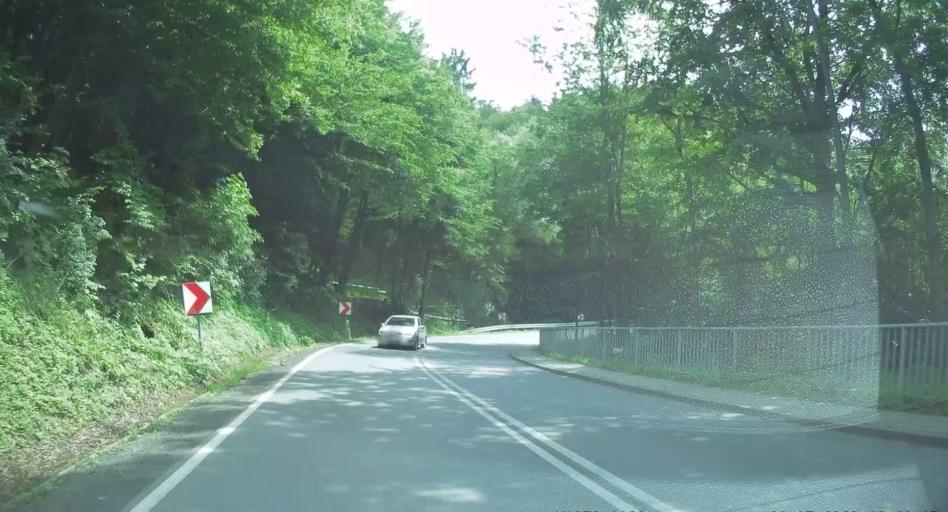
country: PL
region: Lesser Poland Voivodeship
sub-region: Powiat nowosadecki
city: Muszyna
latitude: 49.3533
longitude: 20.8121
